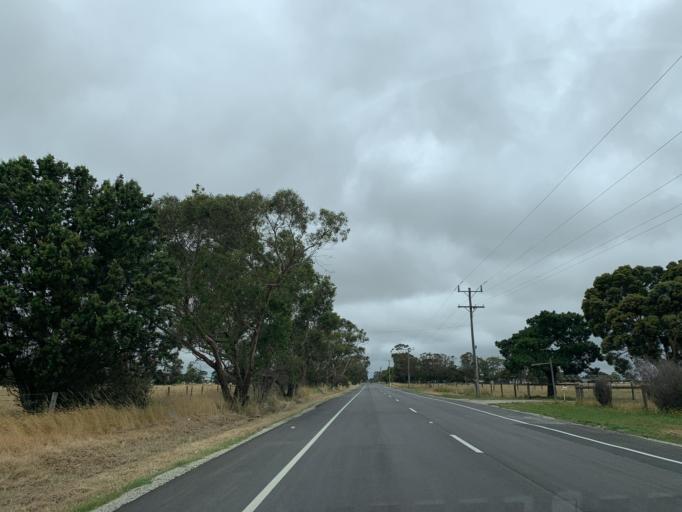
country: AU
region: Victoria
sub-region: Cardinia
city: Officer South
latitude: -38.1412
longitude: 145.3856
